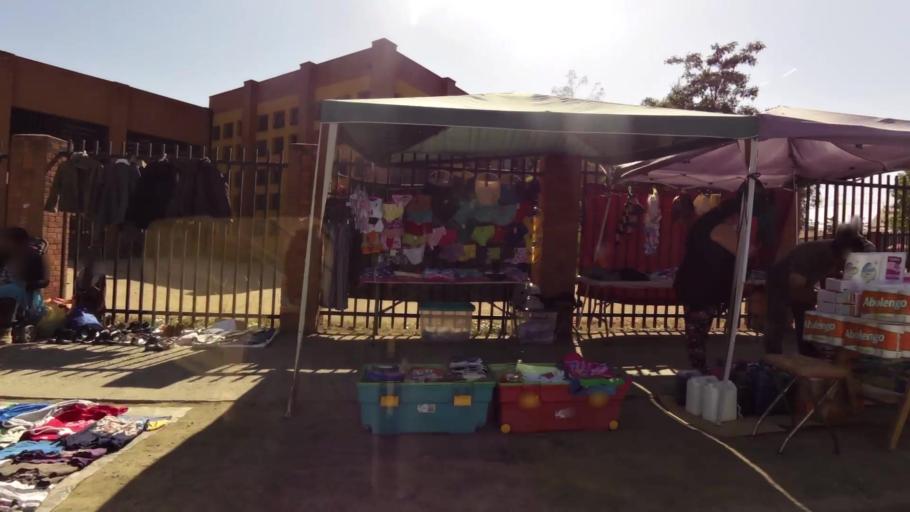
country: CL
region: Maule
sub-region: Provincia de Talca
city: Talca
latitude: -35.4036
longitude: -71.6488
